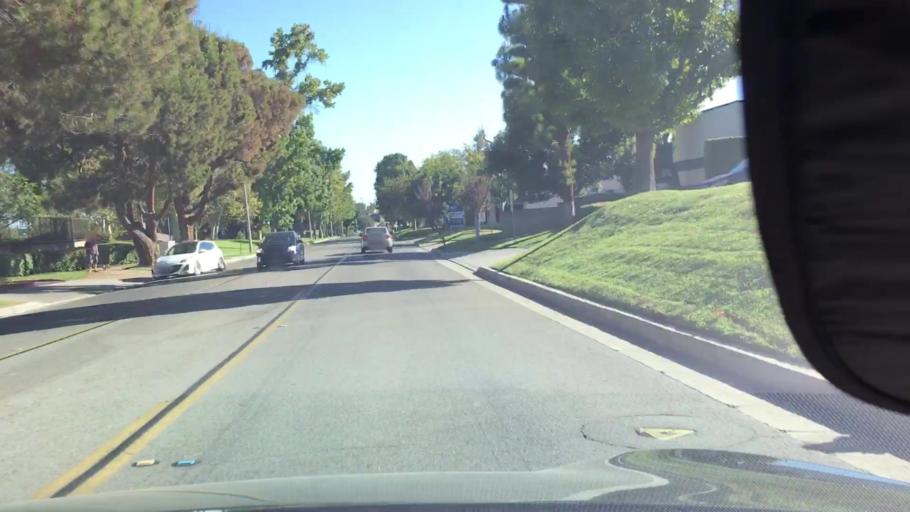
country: US
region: California
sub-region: Orange County
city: Brea
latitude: 33.9279
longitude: -117.9002
